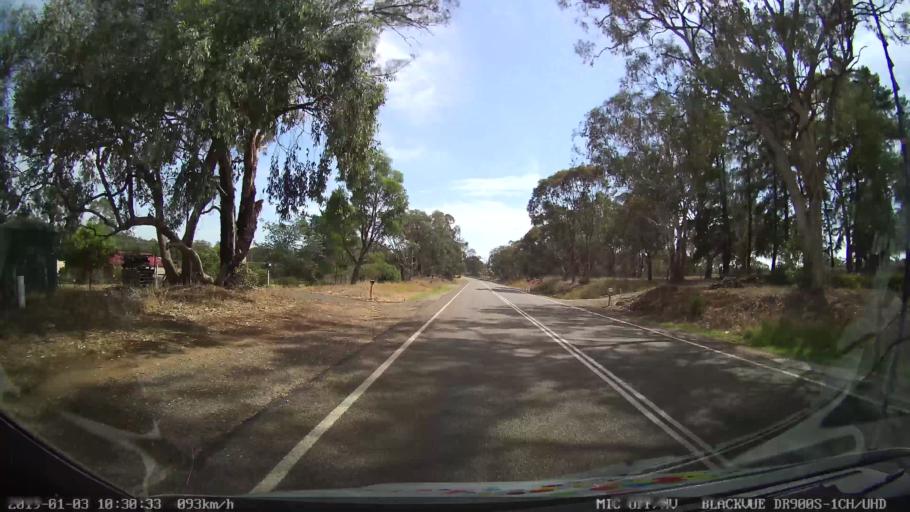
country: AU
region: New South Wales
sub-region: Young
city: Young
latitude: -34.3610
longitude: 148.2695
